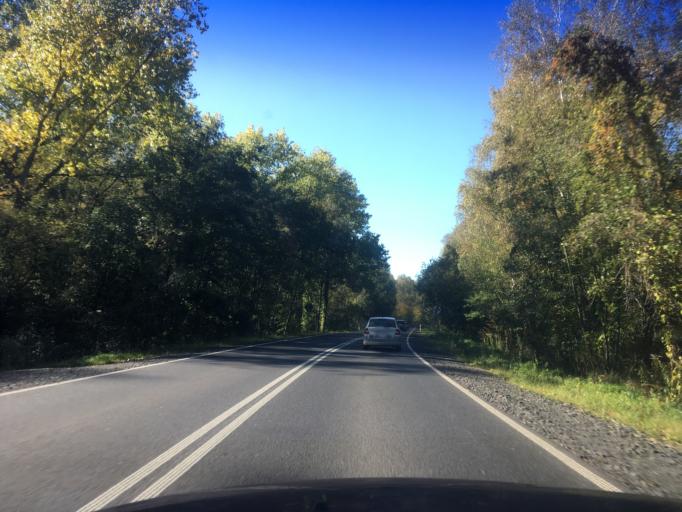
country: DE
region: Saxony
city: Hirschfelde
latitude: 50.9338
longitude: 14.8901
